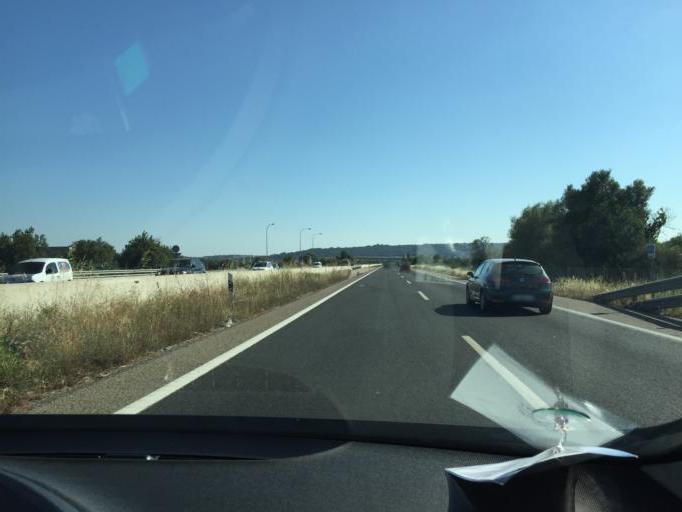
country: ES
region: Balearic Islands
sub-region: Illes Balears
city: Consell
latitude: 39.6542
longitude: 2.8007
